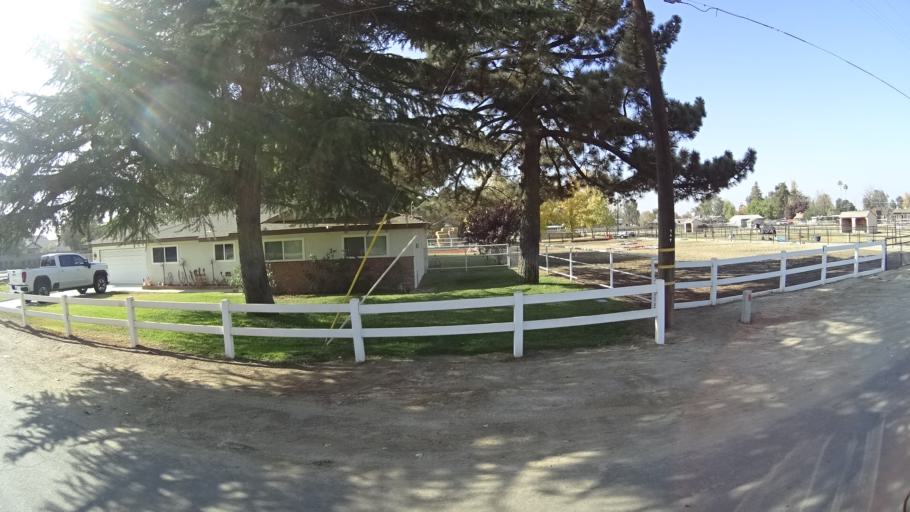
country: US
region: California
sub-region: Kern County
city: Rosedale
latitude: 35.3621
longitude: -119.1655
